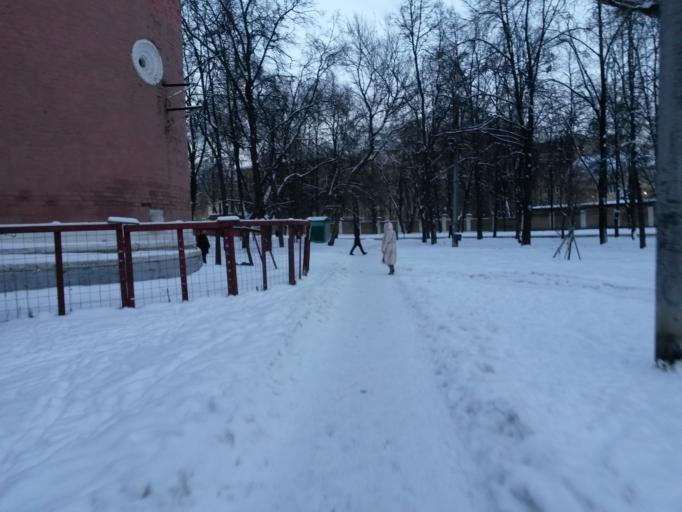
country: RU
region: Moscow
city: Novyye Cheremushki
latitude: 55.7158
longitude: 37.6038
